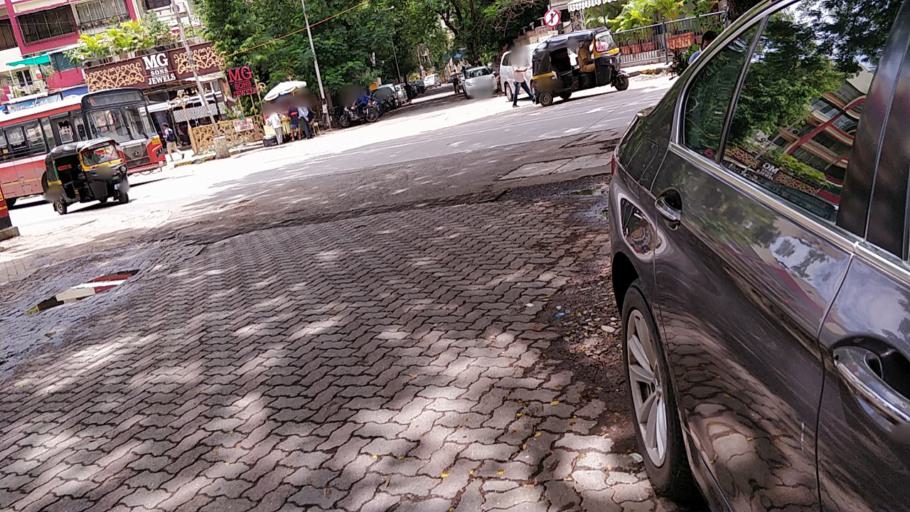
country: IN
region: Maharashtra
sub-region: Mumbai Suburban
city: Mumbai
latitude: 19.0720
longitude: 72.8330
